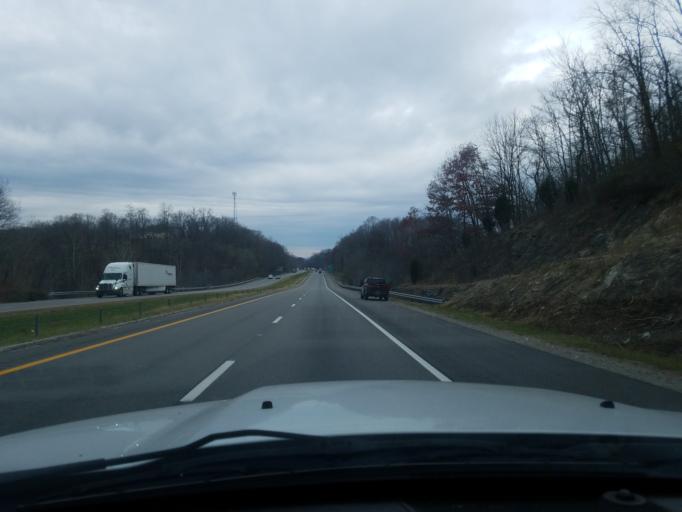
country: US
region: Ohio
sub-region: Lawrence County
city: Burlington
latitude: 38.3948
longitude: -82.5273
